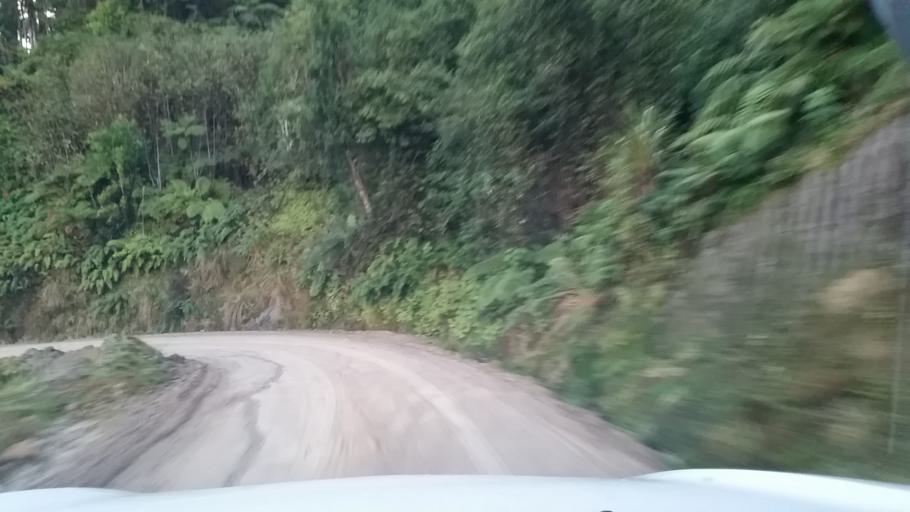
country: NZ
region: Manawatu-Wanganui
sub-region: Wanganui District
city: Wanganui
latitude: -39.7542
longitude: 174.8881
